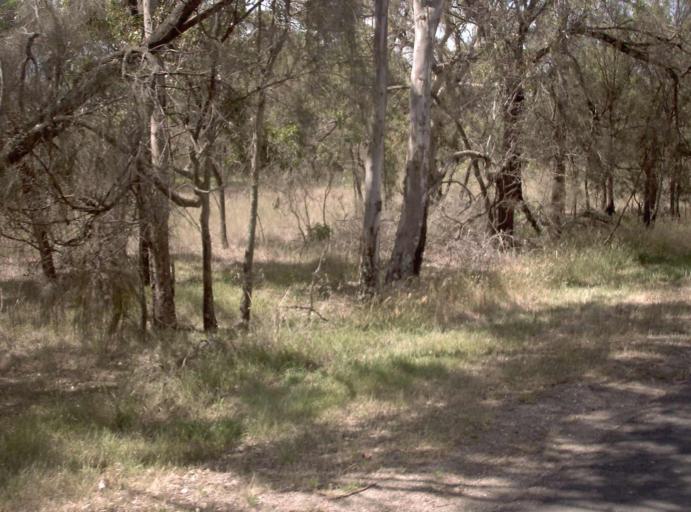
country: AU
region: Victoria
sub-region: Wellington
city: Sale
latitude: -37.9483
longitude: 147.1174
